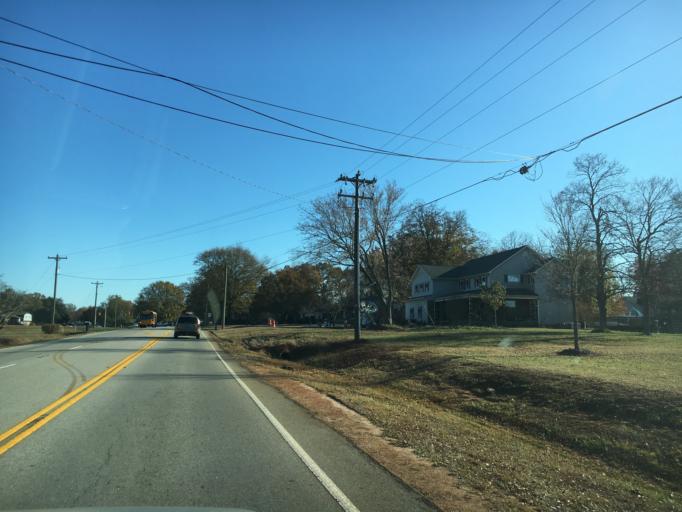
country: US
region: South Carolina
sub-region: Spartanburg County
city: Duncan
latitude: 34.9773
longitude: -82.1608
